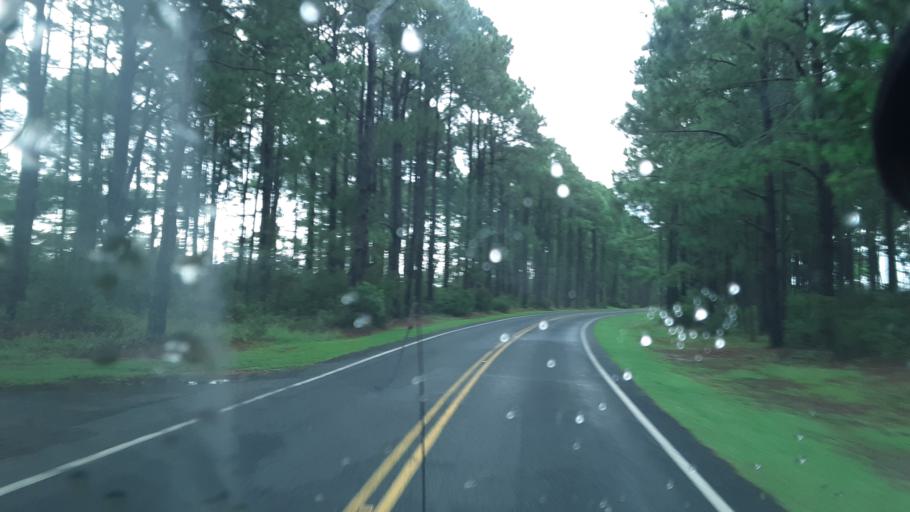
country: US
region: North Carolina
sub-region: Dare County
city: Wanchese
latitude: 35.8208
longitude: -75.5655
